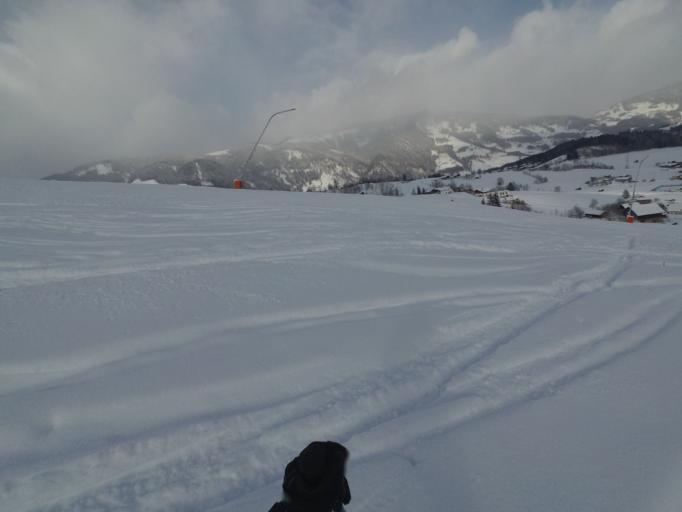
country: AT
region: Salzburg
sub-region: Politischer Bezirk Sankt Johann im Pongau
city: Goldegg
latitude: 47.3109
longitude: 13.0776
